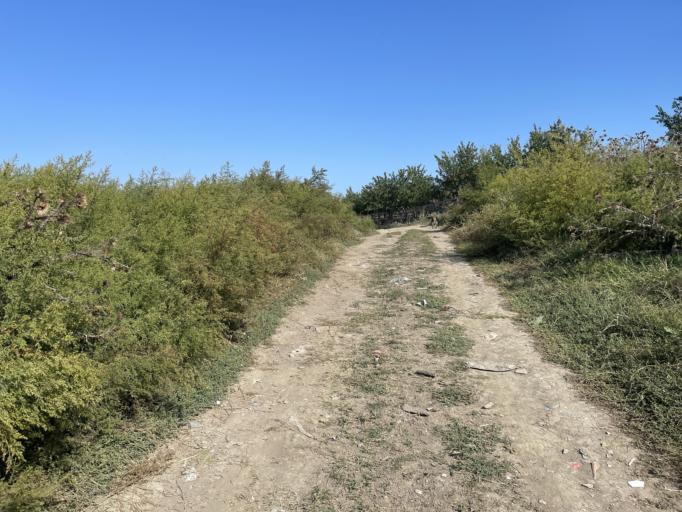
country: RO
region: Iasi
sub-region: Comuna Dumesti
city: Pausesti
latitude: 47.1531
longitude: 27.3155
